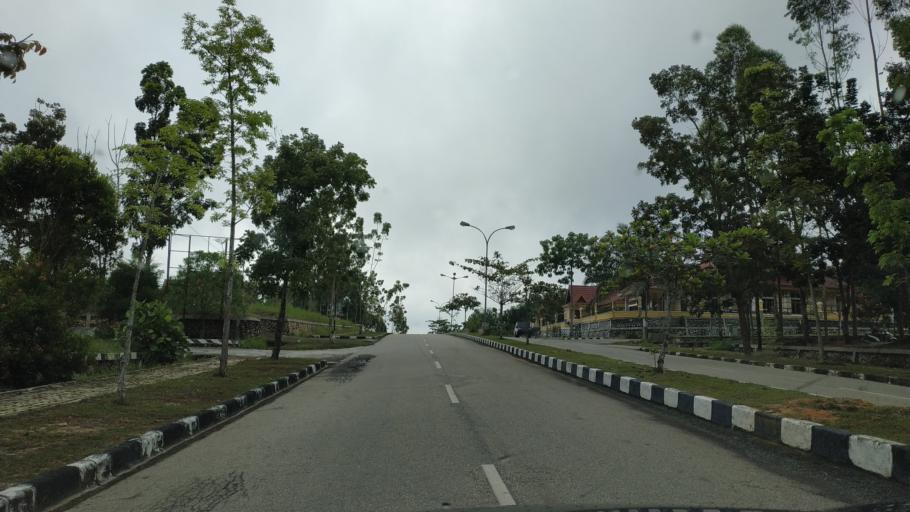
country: ID
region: Riau
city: Pangkalanbunut
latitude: 0.3806
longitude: 101.8260
